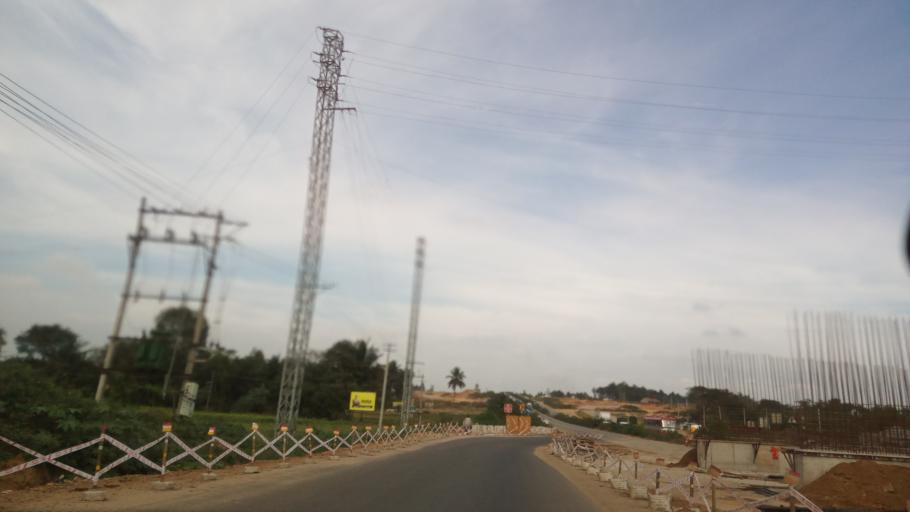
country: IN
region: Karnataka
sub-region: Mandya
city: Shrirangapattana
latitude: 12.4690
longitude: 76.7555
